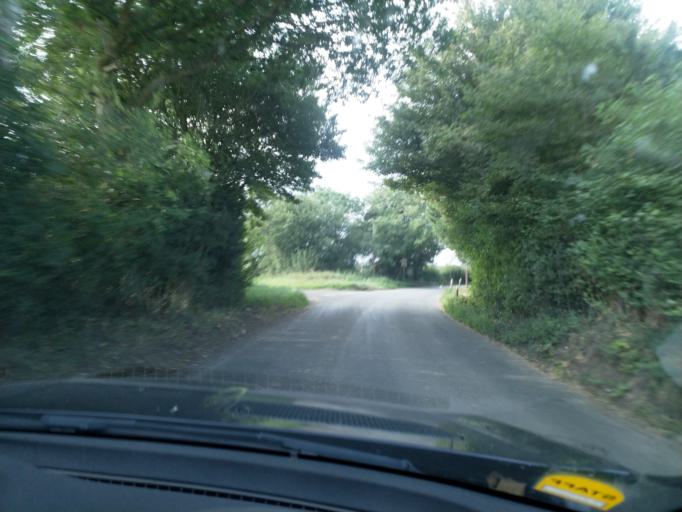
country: GB
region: England
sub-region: Suffolk
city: Elmswell
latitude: 52.2303
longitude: 0.9457
